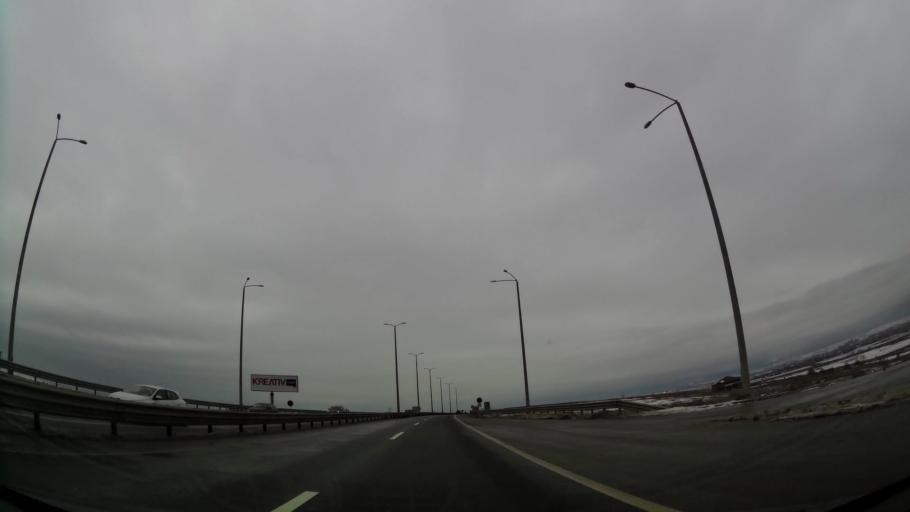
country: XK
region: Pristina
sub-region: Kosovo Polje
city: Kosovo Polje
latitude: 42.6276
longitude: 21.1335
